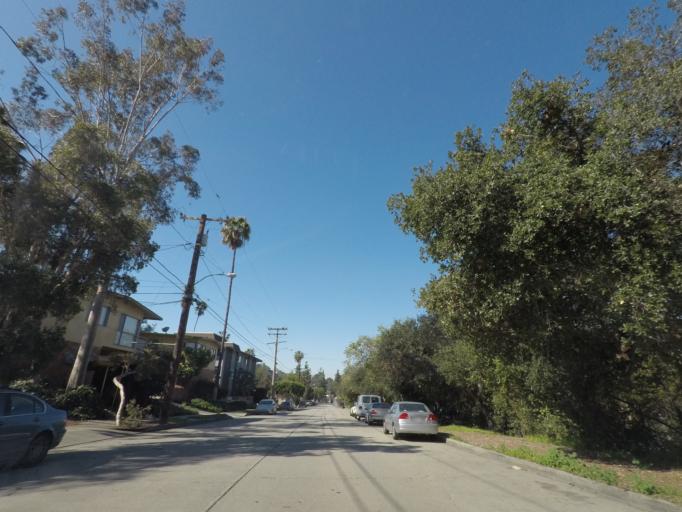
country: US
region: California
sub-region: Los Angeles County
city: South Pasadena
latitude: 34.1143
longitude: -118.1690
